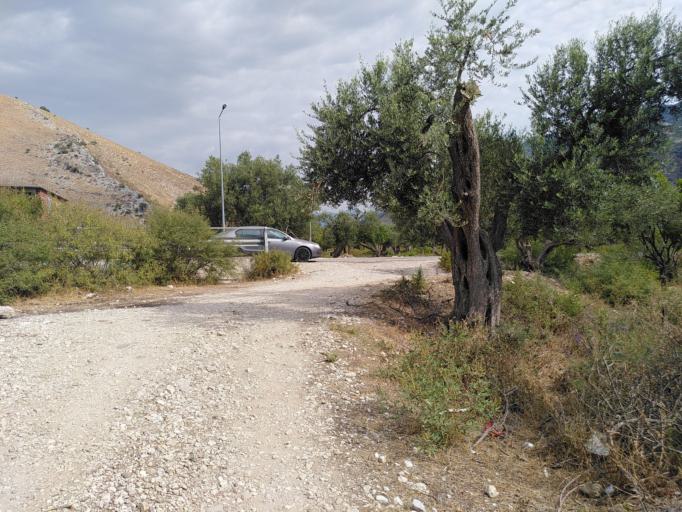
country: AL
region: Vlore
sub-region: Rrethi i Vlores
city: Himare
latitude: 40.0564
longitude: 19.8187
